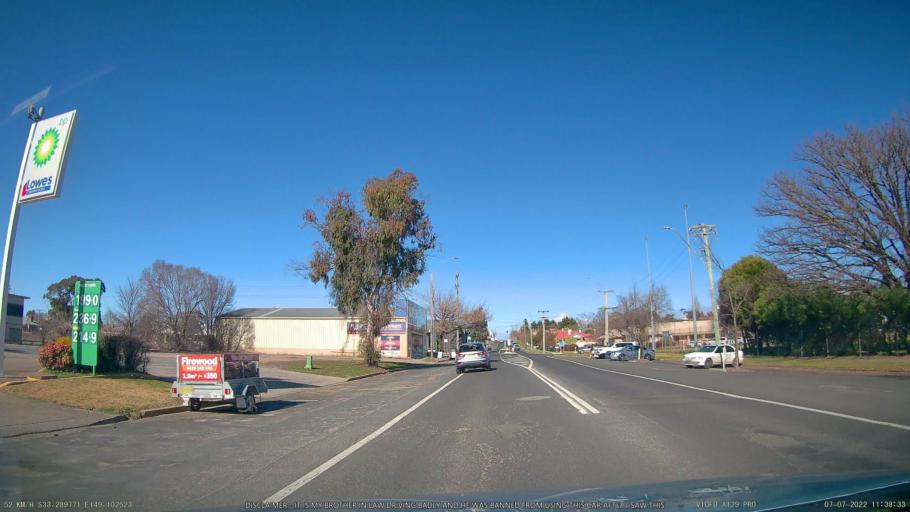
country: AU
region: New South Wales
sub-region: Orange Municipality
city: Orange
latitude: -33.2901
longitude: 149.1025
